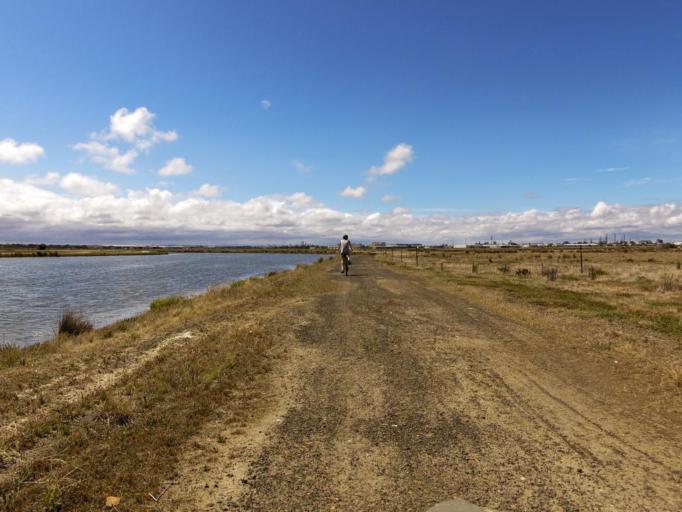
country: AU
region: Victoria
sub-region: Hobsons Bay
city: Altona Meadows
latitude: -37.8729
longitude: 144.7989
